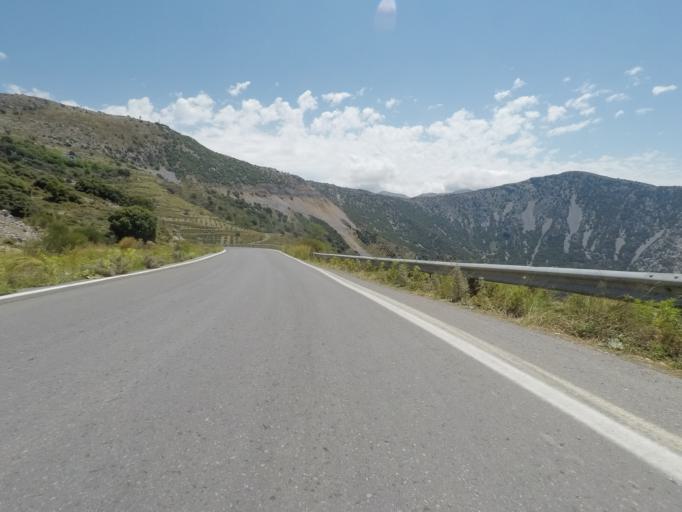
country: GR
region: Crete
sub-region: Nomos Irakleiou
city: Mokhos
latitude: 35.2153
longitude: 25.4604
